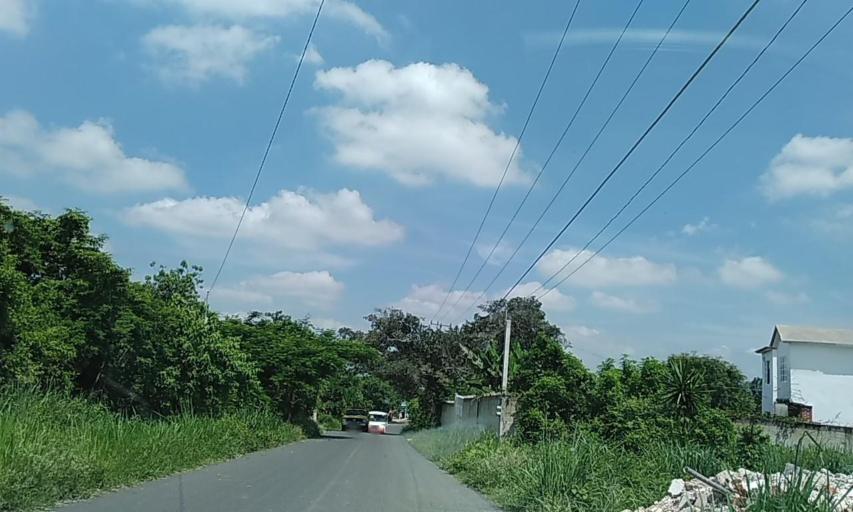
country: MX
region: Veracruz
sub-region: Emiliano Zapata
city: Dos Rios
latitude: 19.4389
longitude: -96.7798
